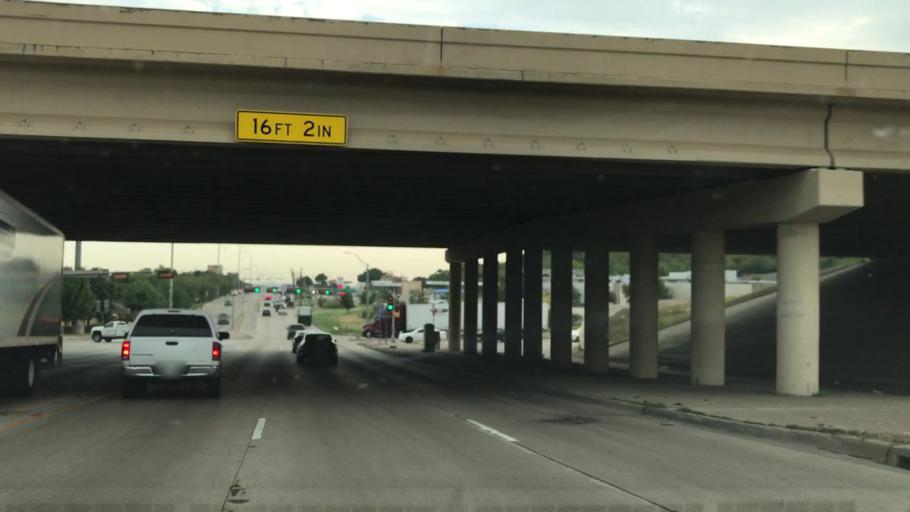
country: US
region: Texas
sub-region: Dallas County
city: Cockrell Hill
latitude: 32.7671
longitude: -96.8739
